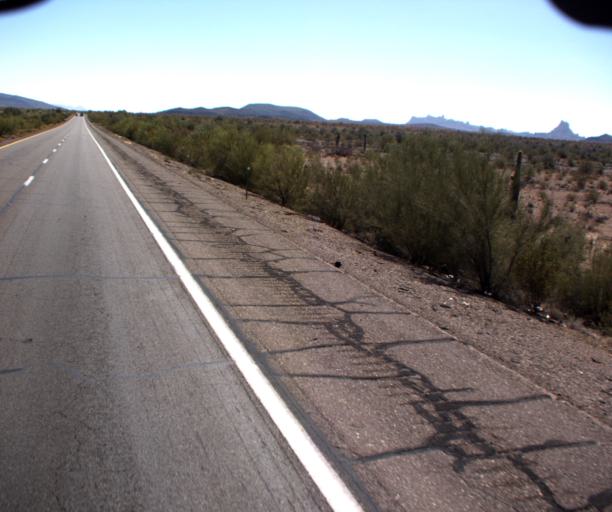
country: US
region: Arizona
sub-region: La Paz County
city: Quartzsite
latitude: 33.6594
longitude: -113.9934
